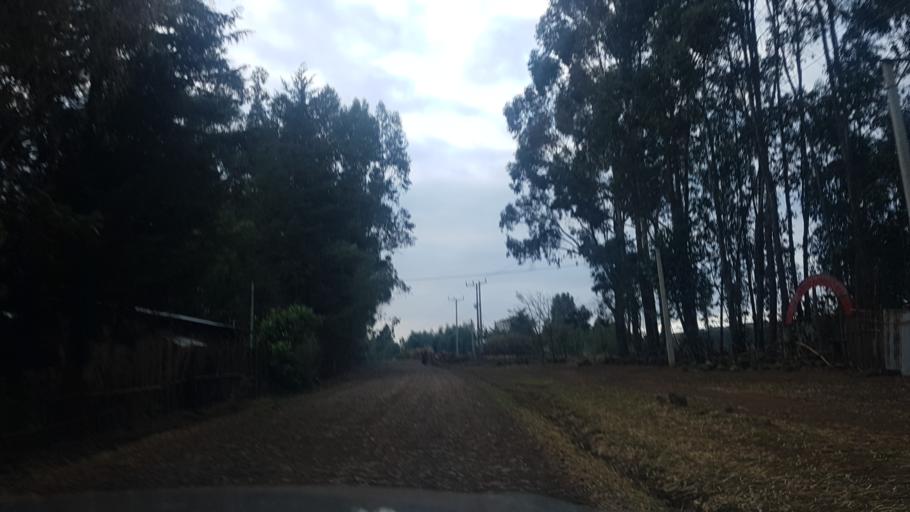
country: ET
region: Amhara
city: Finote Selam
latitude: 10.8134
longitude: 37.6488
